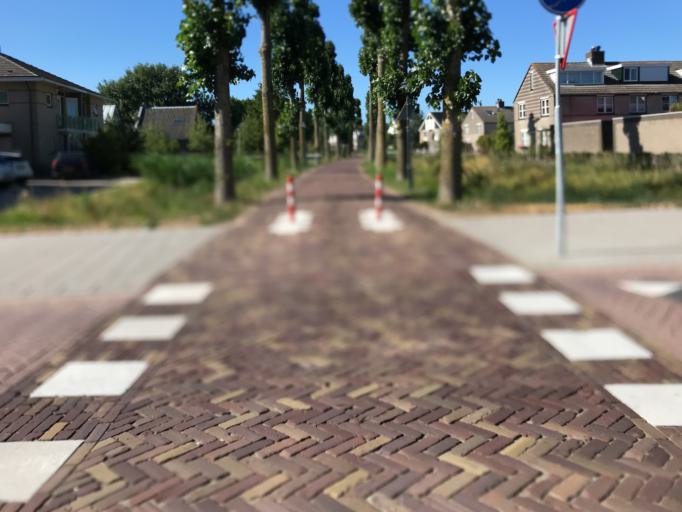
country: NL
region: North Holland
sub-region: Gemeente Diemen
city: Diemen
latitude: 52.3512
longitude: 4.9716
